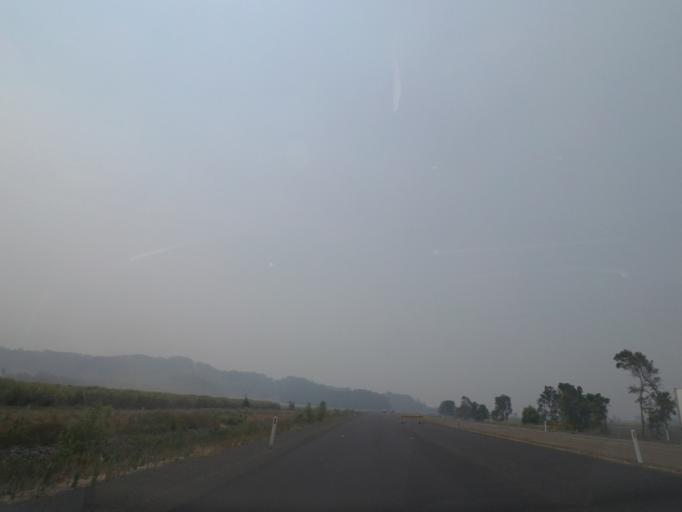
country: AU
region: New South Wales
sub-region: Ballina
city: Ballina
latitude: -28.8892
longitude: 153.4823
